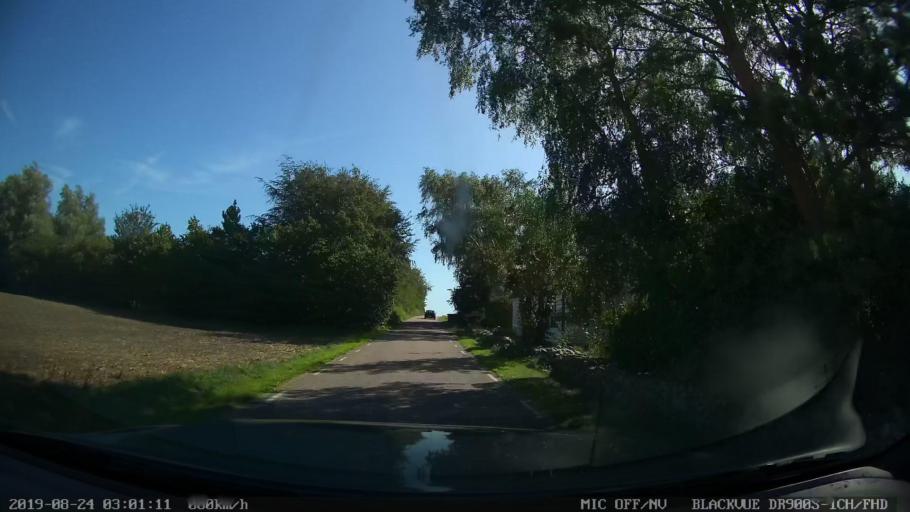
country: SE
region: Skane
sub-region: Skurups Kommun
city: Skurup
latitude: 55.4485
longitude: 13.4348
